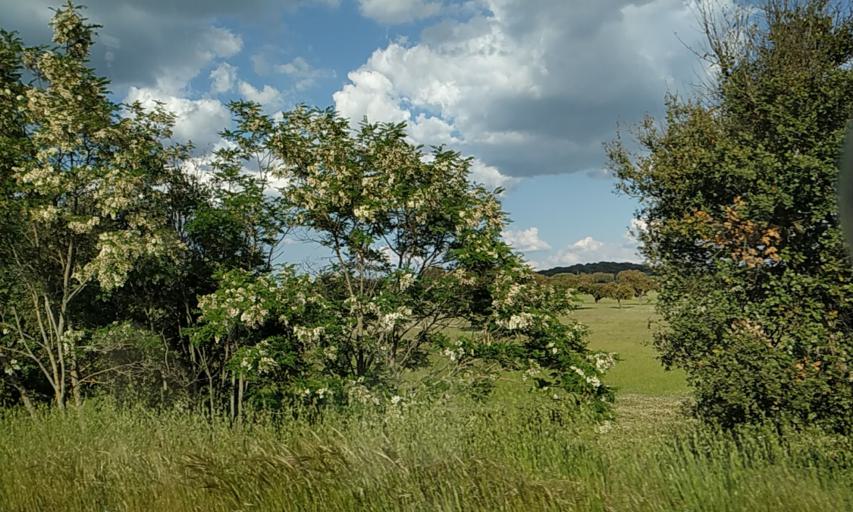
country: PT
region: Portalegre
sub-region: Portalegre
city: Urra
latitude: 39.2052
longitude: -7.4585
